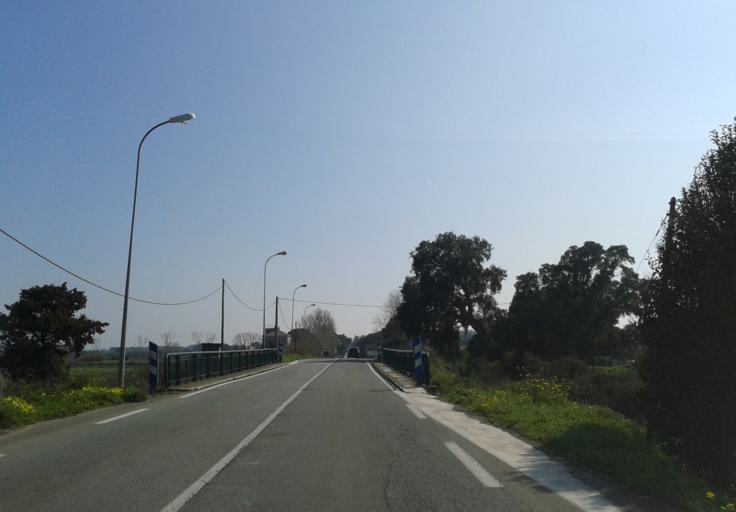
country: FR
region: Corsica
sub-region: Departement de la Haute-Corse
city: Cervione
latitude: 42.3127
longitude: 9.5418
